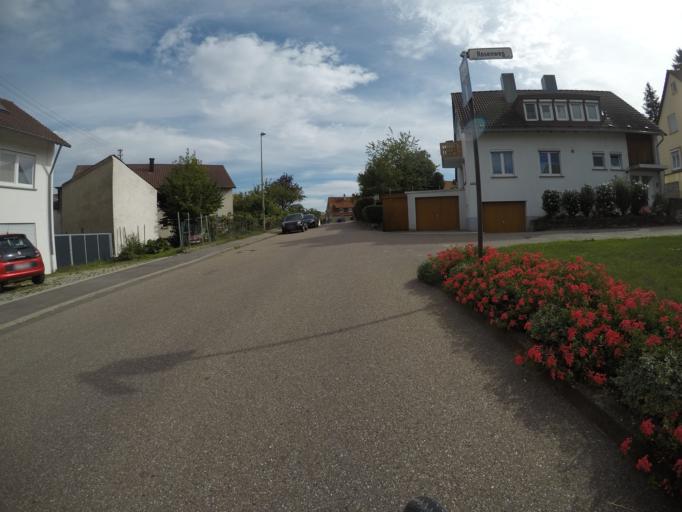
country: DE
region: Baden-Wuerttemberg
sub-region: Regierungsbezirk Stuttgart
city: Vaihingen an der Enz
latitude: 48.9173
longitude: 8.9812
